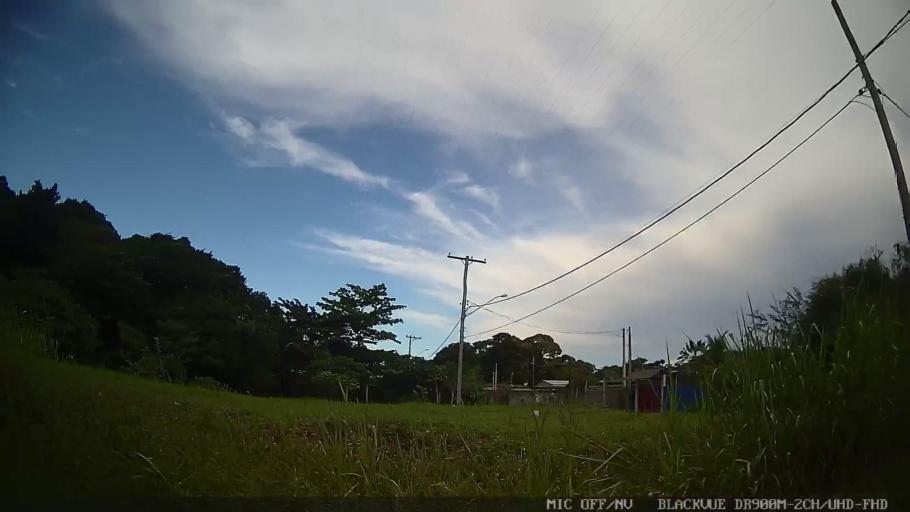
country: BR
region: Sao Paulo
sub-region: Iguape
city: Iguape
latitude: -24.6758
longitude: -47.4531
